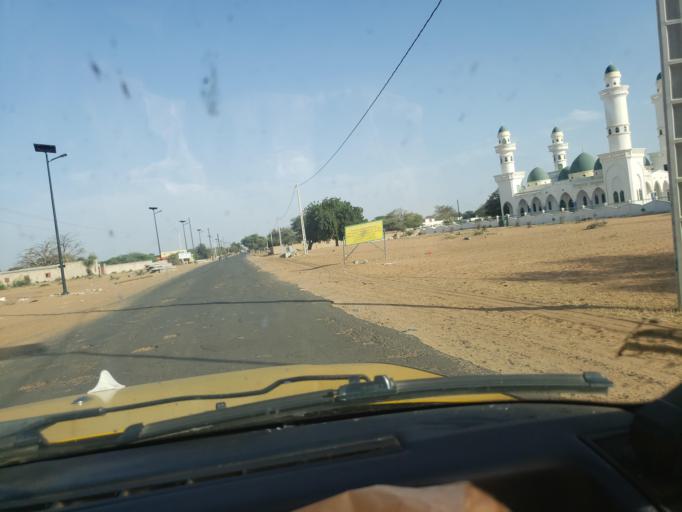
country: SN
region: Louga
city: Louga
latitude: 15.5126
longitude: -15.9938
